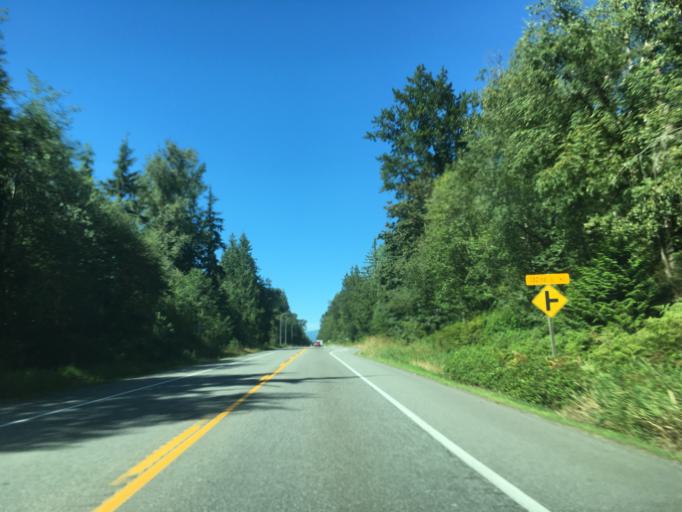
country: US
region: Washington
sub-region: Snohomish County
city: Sisco Heights
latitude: 48.1127
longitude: -122.1124
